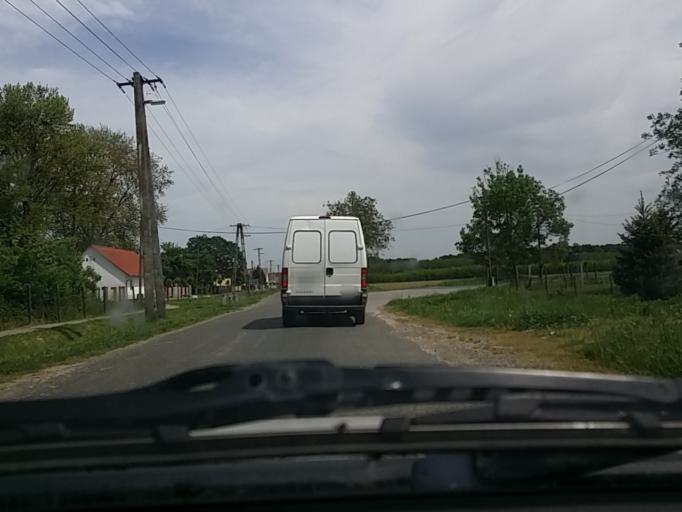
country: HU
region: Somogy
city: Barcs
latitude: 45.9535
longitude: 17.6197
